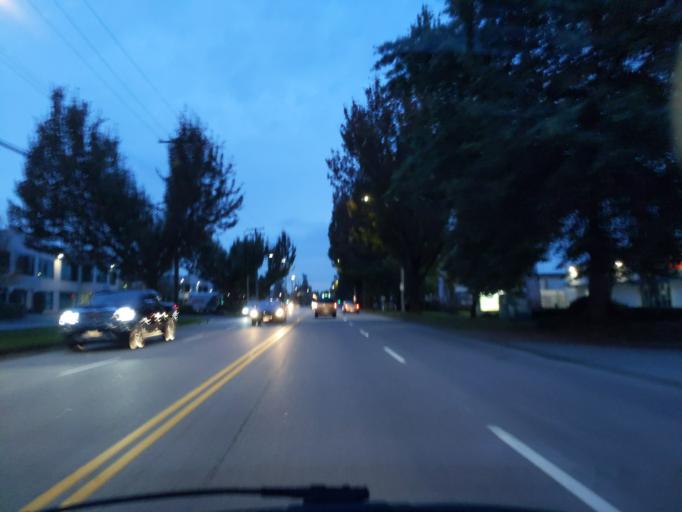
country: CA
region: British Columbia
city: Pitt Meadows
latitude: 49.1770
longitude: -122.6865
